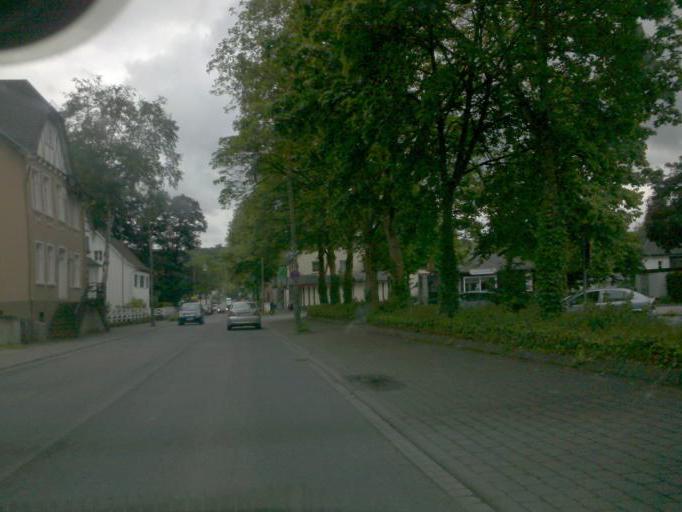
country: DE
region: North Rhine-Westphalia
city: Eslohe
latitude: 51.2559
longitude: 8.1722
